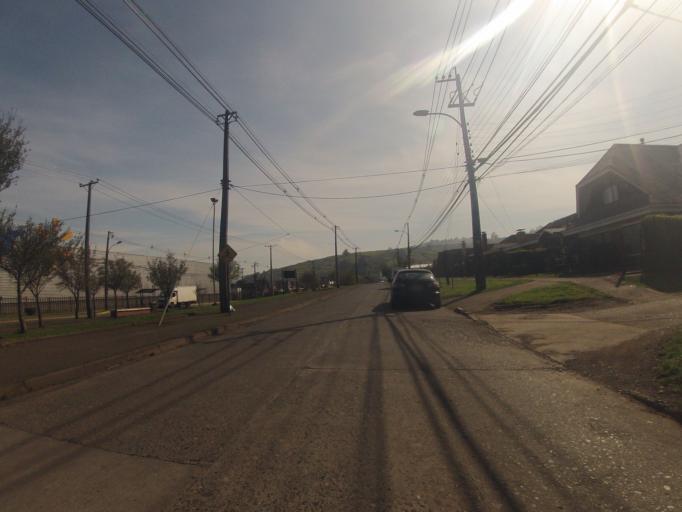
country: CL
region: Araucania
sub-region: Provincia de Cautin
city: Temuco
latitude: -38.7294
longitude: -72.5993
